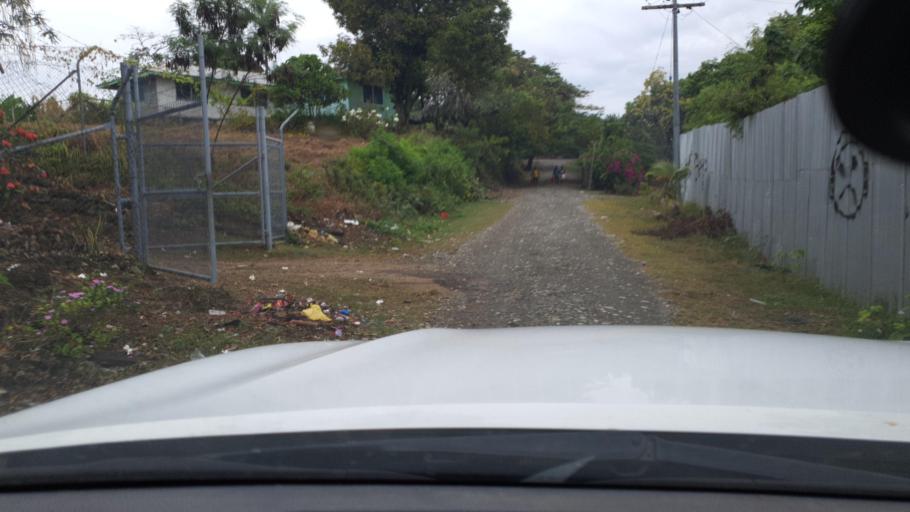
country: SB
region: Guadalcanal
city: Honiara
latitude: -9.4413
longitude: 159.9773
